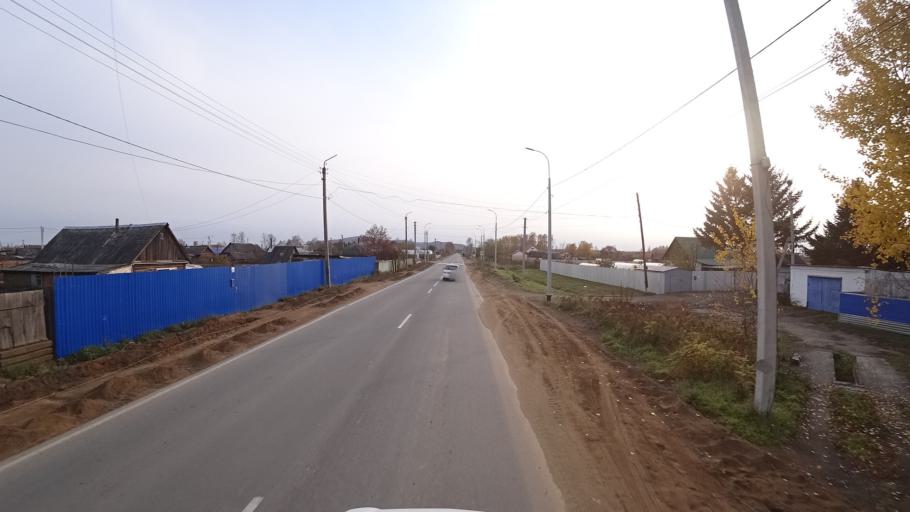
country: RU
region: Khabarovsk Krai
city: Amursk
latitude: 50.0866
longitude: 136.4996
